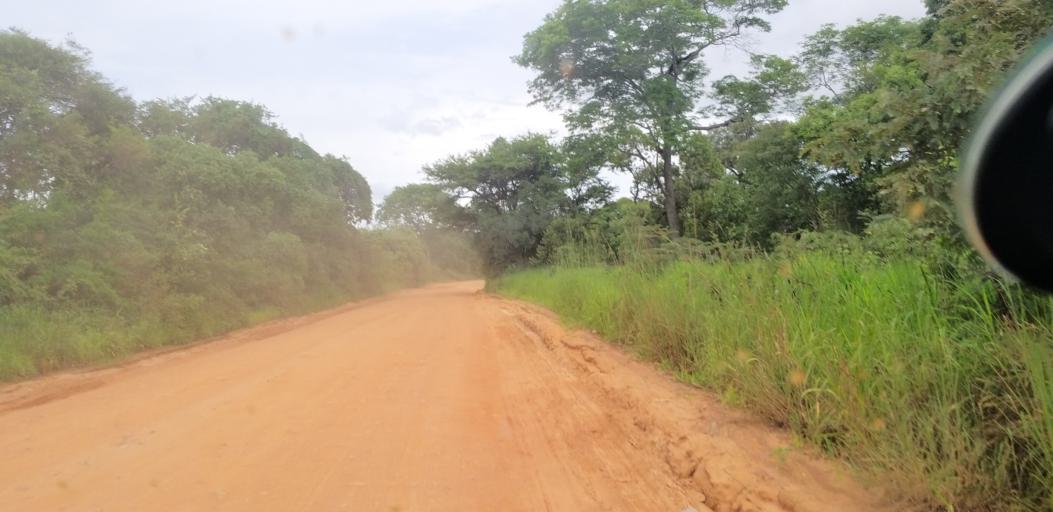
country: ZM
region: Lusaka
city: Lusaka
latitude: -15.1998
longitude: 28.4399
